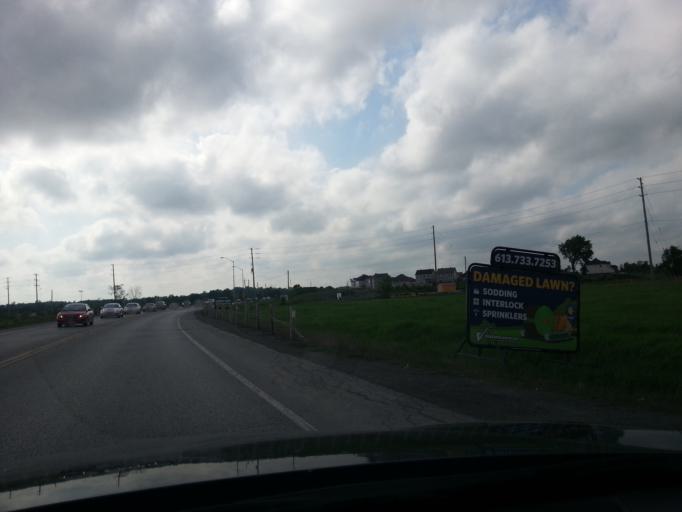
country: CA
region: Ontario
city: Bells Corners
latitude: 45.2597
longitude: -75.7701
